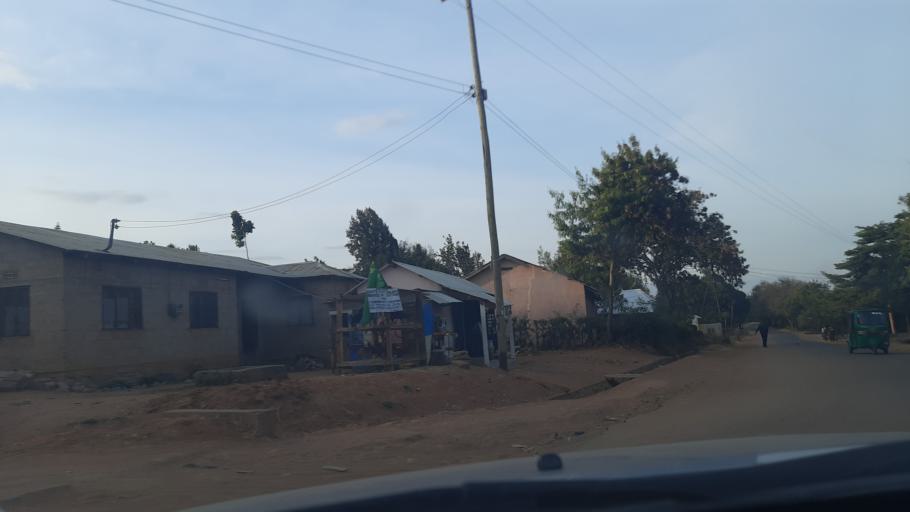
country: TZ
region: Singida
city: Singida
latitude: -4.8147
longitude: 34.7314
